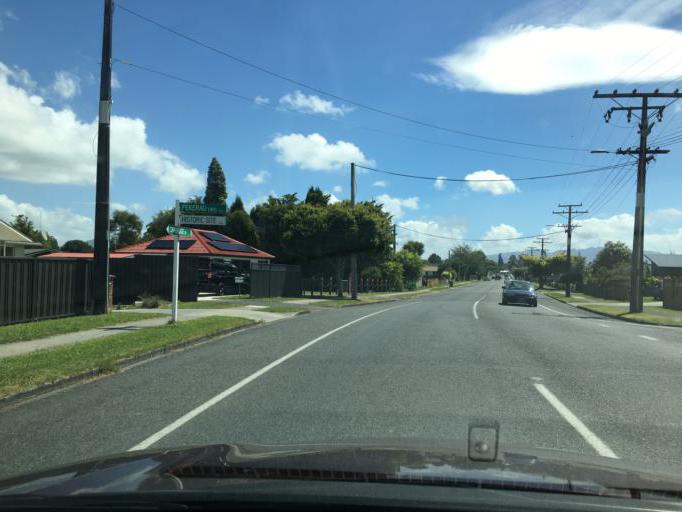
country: NZ
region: Waikato
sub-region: Waipa District
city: Cambridge
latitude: -38.0070
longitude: 175.3365
